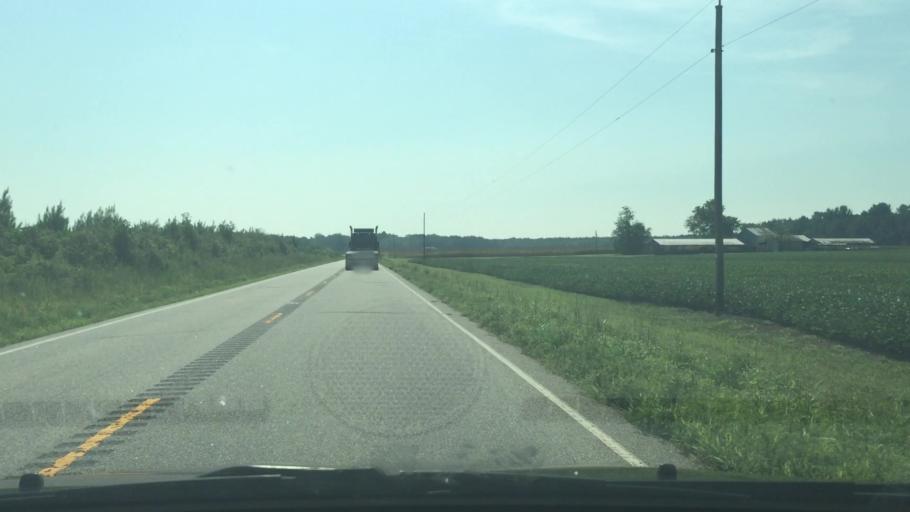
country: US
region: Virginia
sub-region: Sussex County
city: Sussex
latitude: 36.9792
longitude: -77.2314
